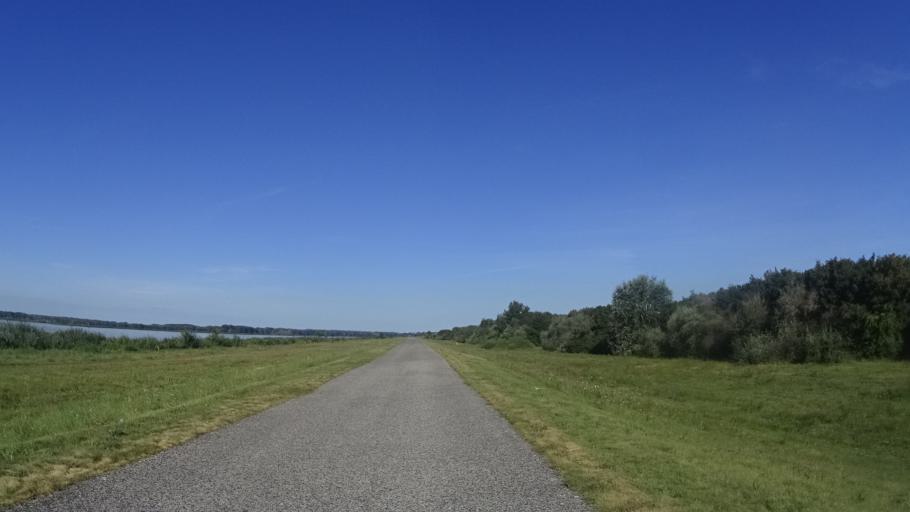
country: SK
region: Bratislavsky
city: Dunajska Luzna
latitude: 48.0590
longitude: 17.2175
